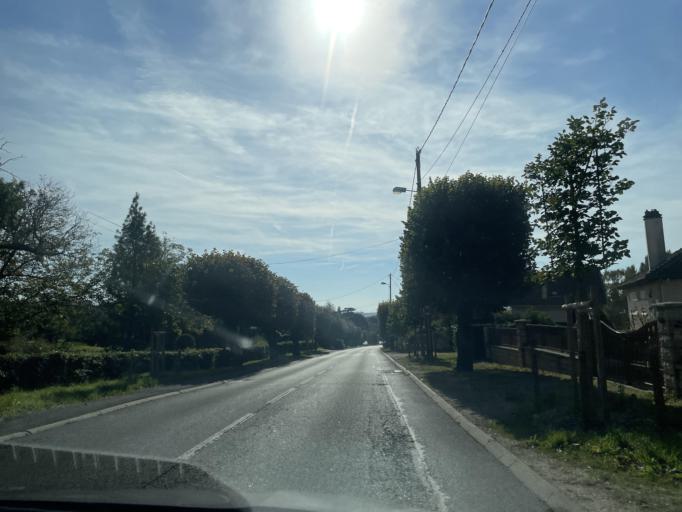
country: FR
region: Ile-de-France
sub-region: Departement de Seine-et-Marne
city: Coulommiers
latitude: 48.8252
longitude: 3.0877
